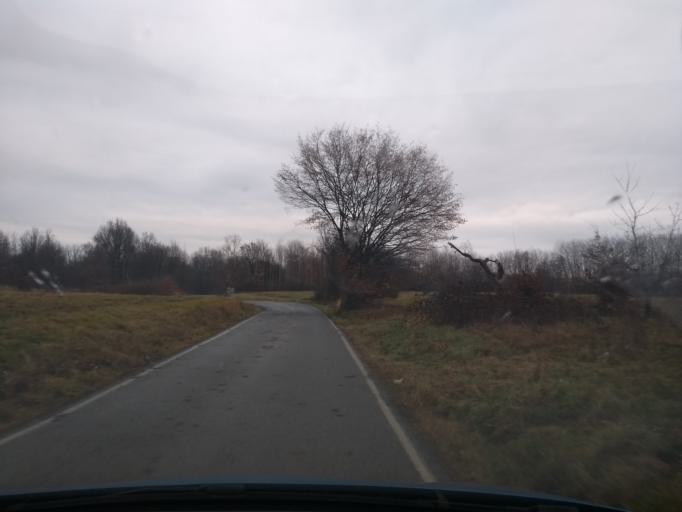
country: IT
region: Piedmont
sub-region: Provincia di Torino
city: Front
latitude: 45.2755
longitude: 7.6498
